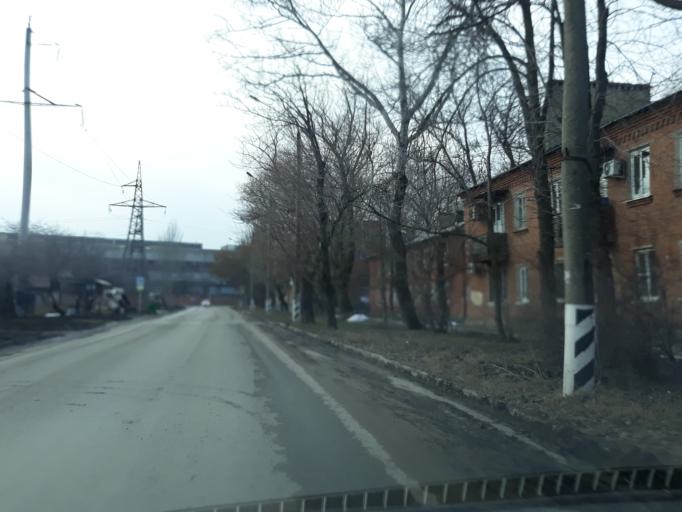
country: RU
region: Rostov
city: Taganrog
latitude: 47.2504
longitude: 38.9070
